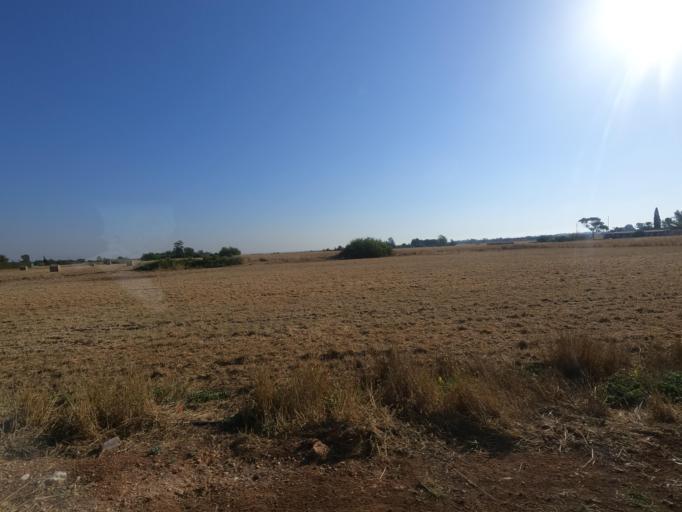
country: CY
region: Ammochostos
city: Frenaros
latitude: 35.0537
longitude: 33.9132
